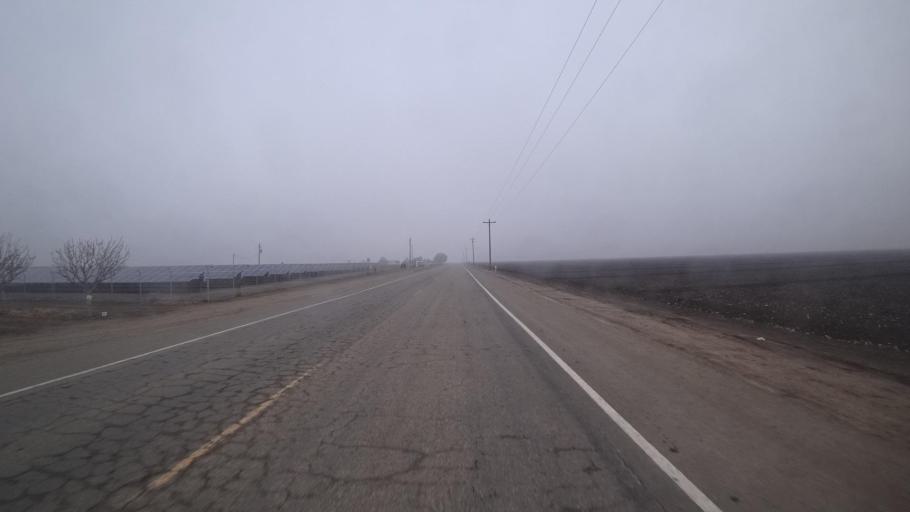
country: US
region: California
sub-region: Kern County
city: Buttonwillow
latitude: 35.4342
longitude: -119.5182
